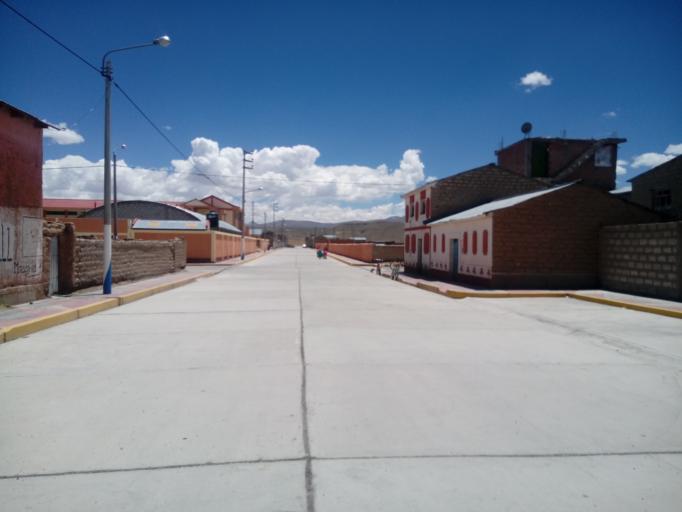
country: PE
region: Puno
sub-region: El Collao
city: Mazo Cruz
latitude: -16.7417
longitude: -69.7138
